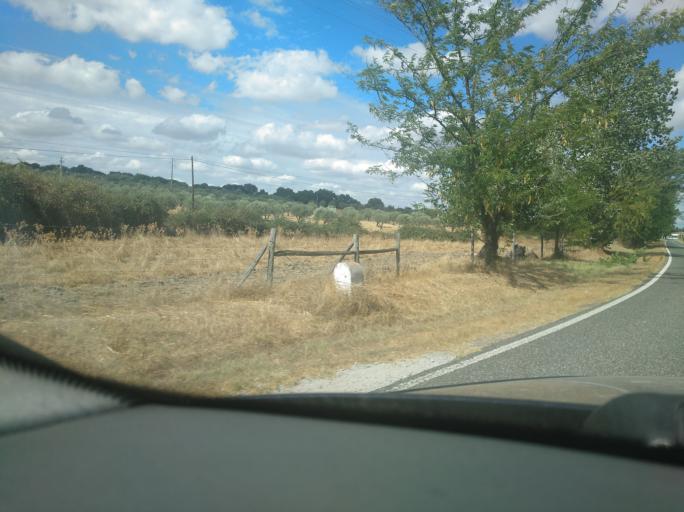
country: PT
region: Portalegre
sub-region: Arronches
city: Arronches
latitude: 39.0847
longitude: -7.3540
